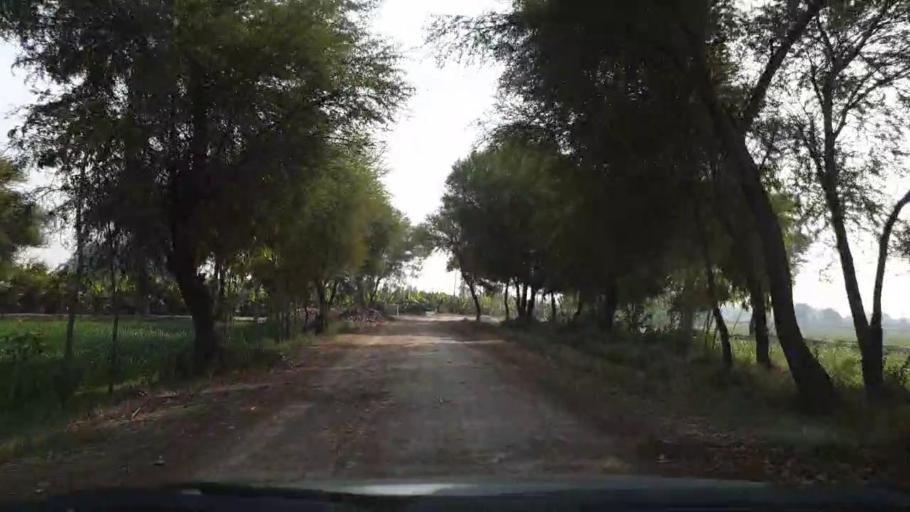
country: PK
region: Sindh
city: Matiari
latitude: 25.6558
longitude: 68.5501
